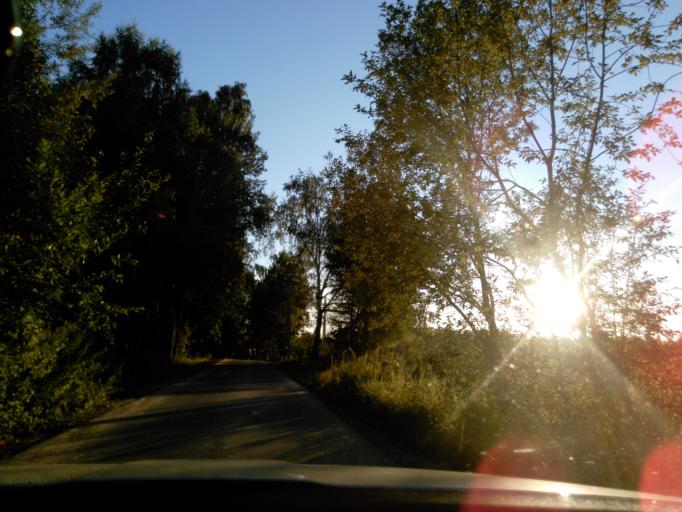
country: RU
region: Moskovskaya
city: Solnechnogorsk
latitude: 56.1280
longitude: 36.8418
